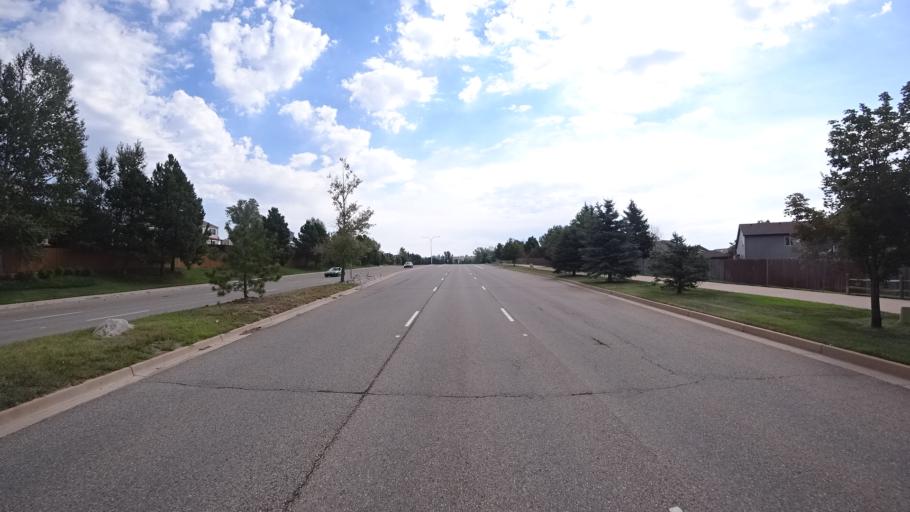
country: US
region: Colorado
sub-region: El Paso County
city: Cimarron Hills
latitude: 38.9110
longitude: -104.7070
